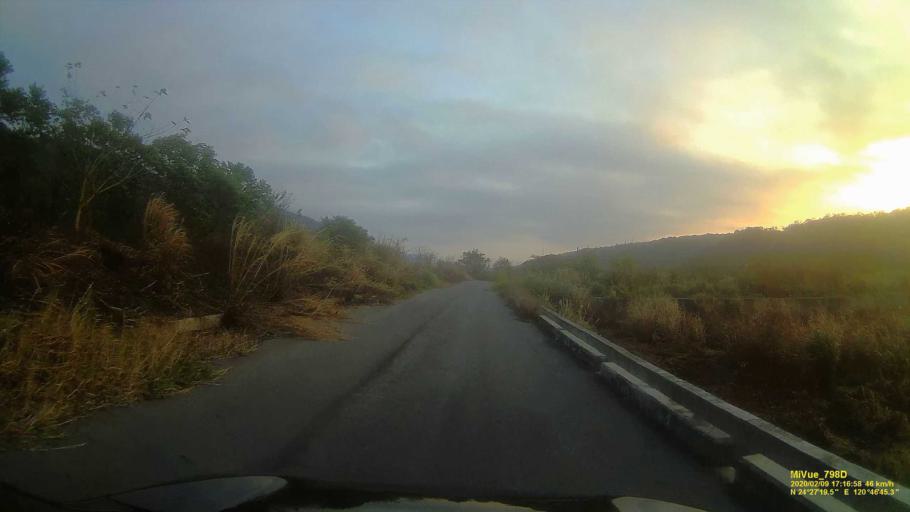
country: TW
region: Taiwan
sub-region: Miaoli
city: Miaoli
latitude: 24.4552
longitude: 120.7792
